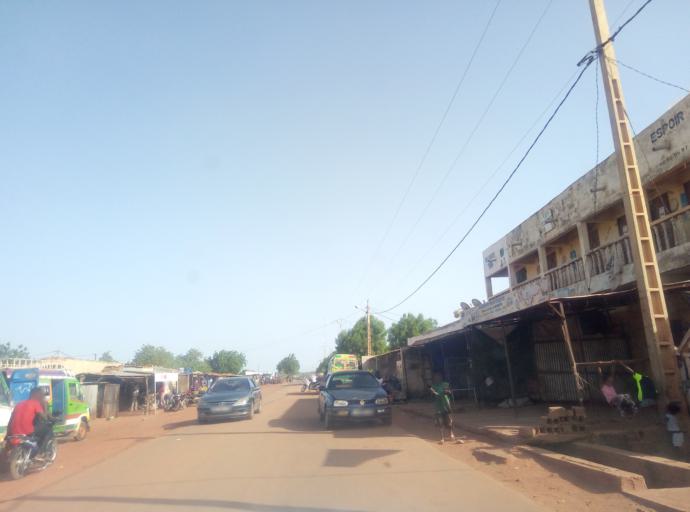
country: ML
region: Bamako
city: Bamako
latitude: 12.6155
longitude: -7.7778
